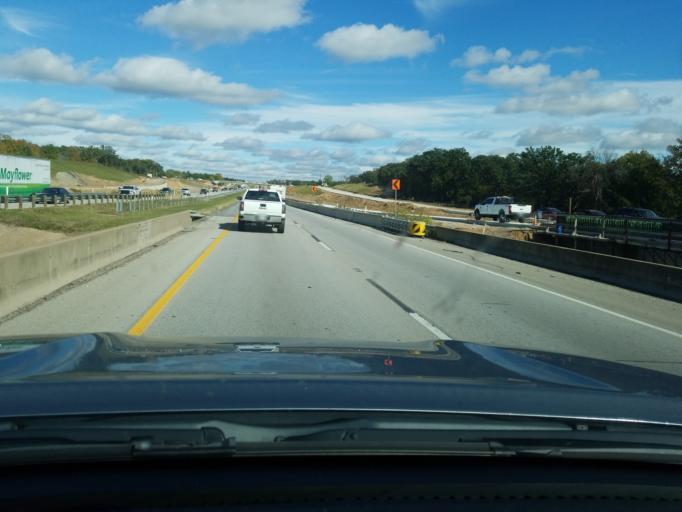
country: US
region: Texas
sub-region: Parker County
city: Hudson Oaks
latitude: 32.7465
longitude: -97.7348
